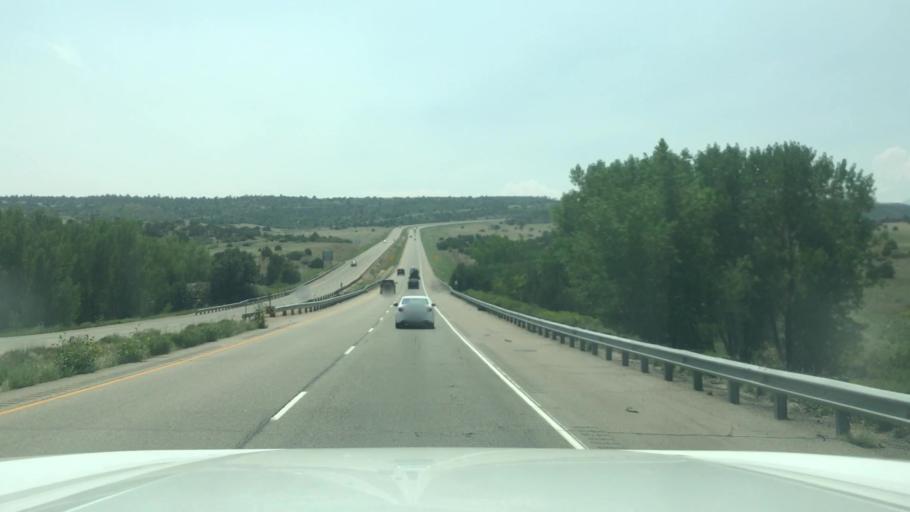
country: US
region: Colorado
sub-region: Pueblo County
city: Colorado City
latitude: 37.9511
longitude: -104.8024
